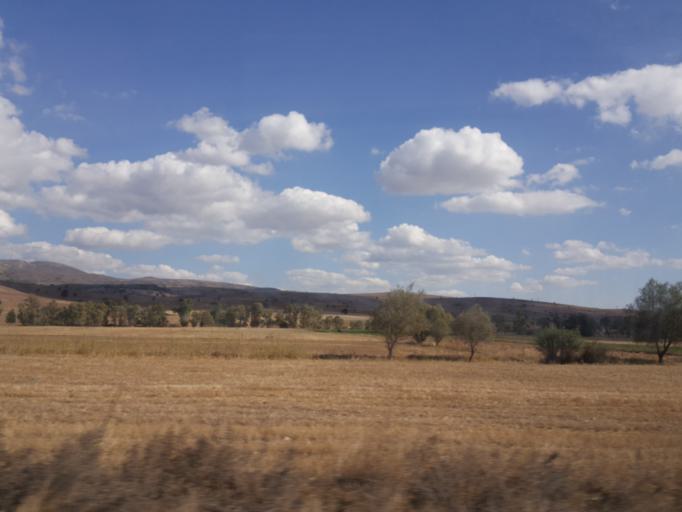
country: TR
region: Tokat
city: Camlibel
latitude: 40.1870
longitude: 36.4541
